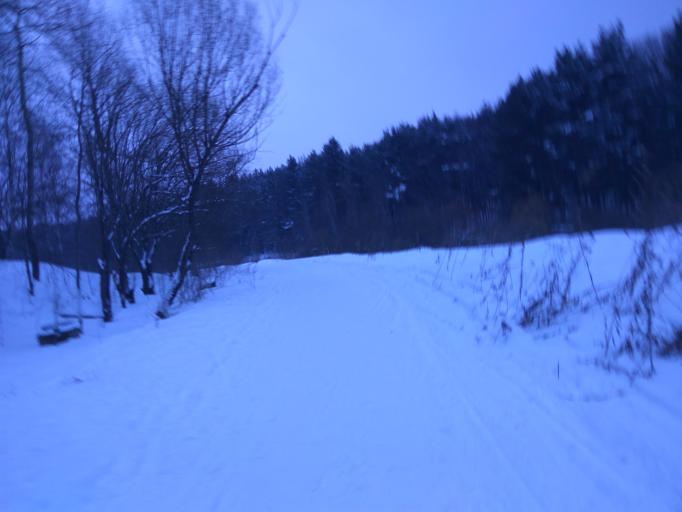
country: RU
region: Moscow
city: Orekhovo-Borisovo Severnoye
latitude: 55.6003
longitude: 37.7023
